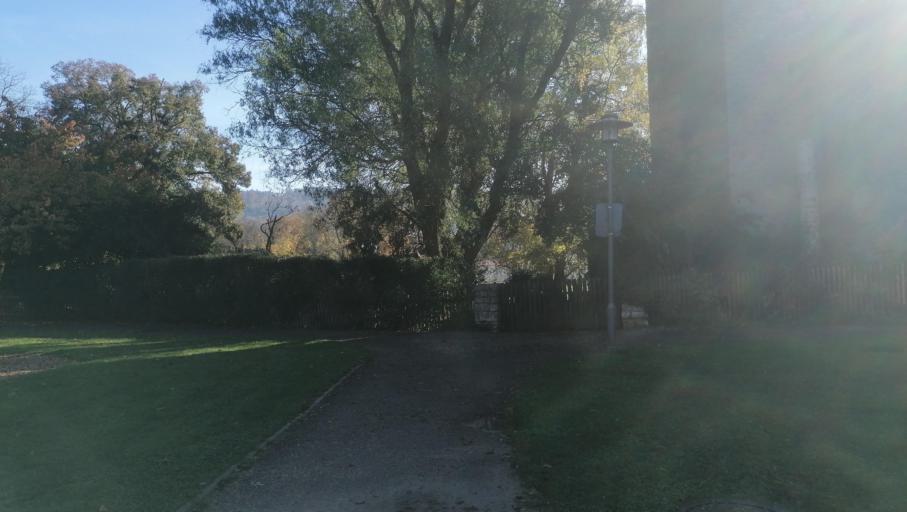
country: DE
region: Bavaria
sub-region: Upper Palatinate
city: Berching
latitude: 49.1084
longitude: 11.4402
